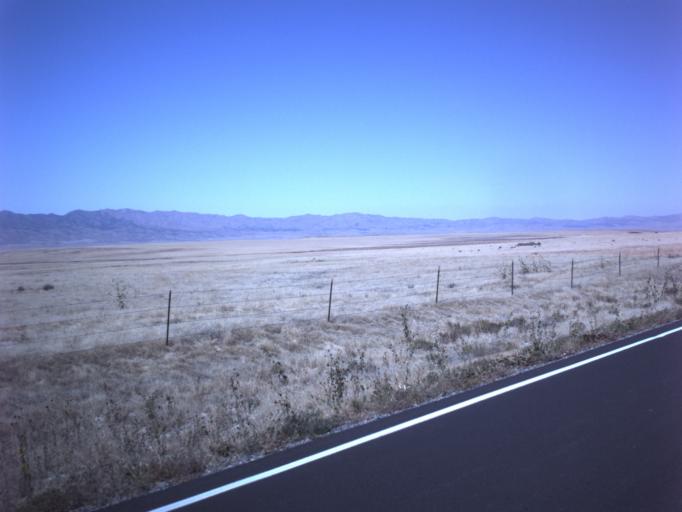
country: US
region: Utah
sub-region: Tooele County
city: Grantsville
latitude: 40.4142
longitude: -112.7486
